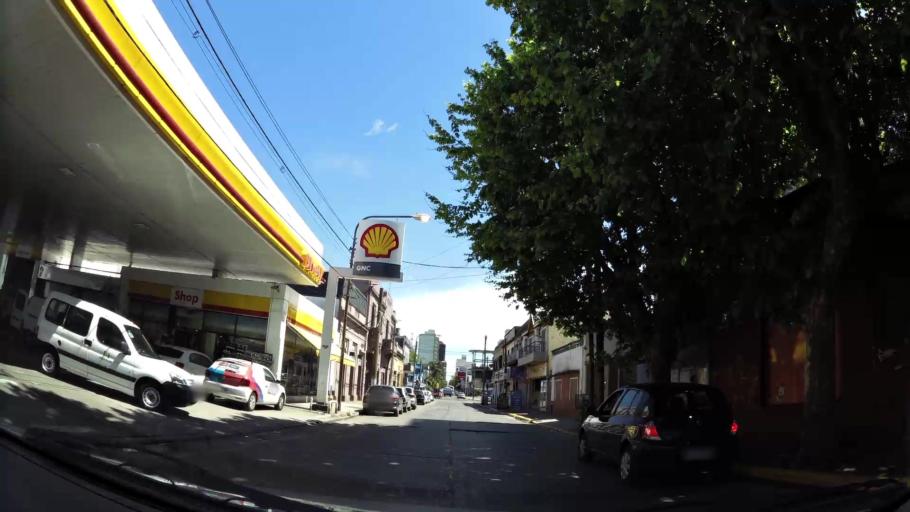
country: AR
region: Buenos Aires
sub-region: Partido de Quilmes
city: Quilmes
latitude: -34.7259
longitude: -58.2507
